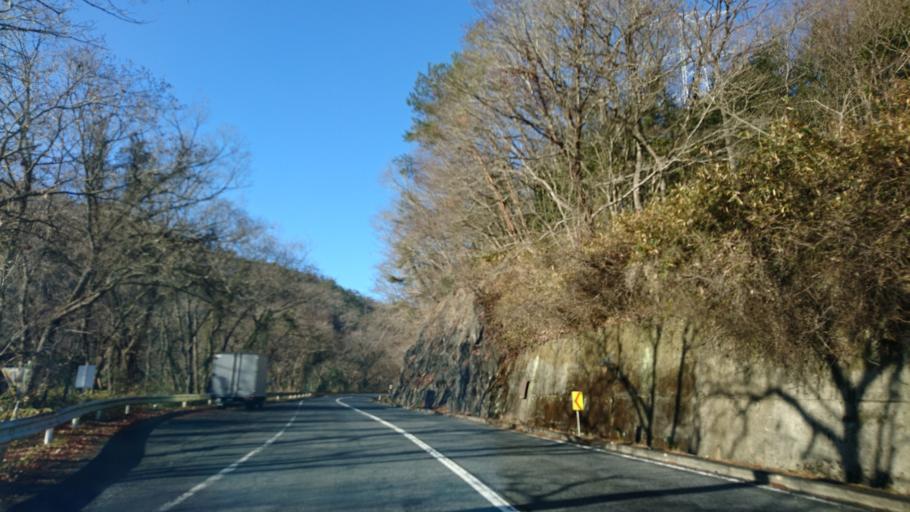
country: JP
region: Okayama
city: Takahashi
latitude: 34.8246
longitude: 133.6708
